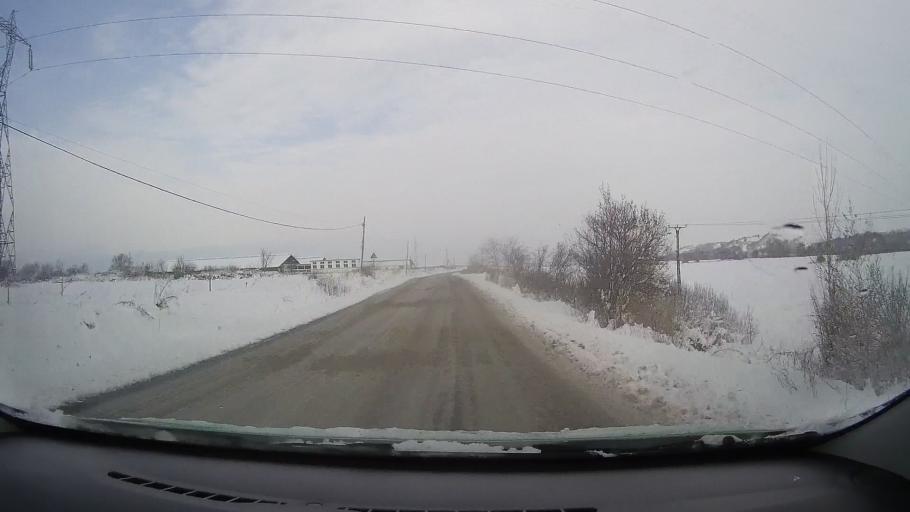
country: RO
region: Alba
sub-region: Comuna Pianu
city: Pianu de Jos
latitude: 45.9513
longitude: 23.4785
